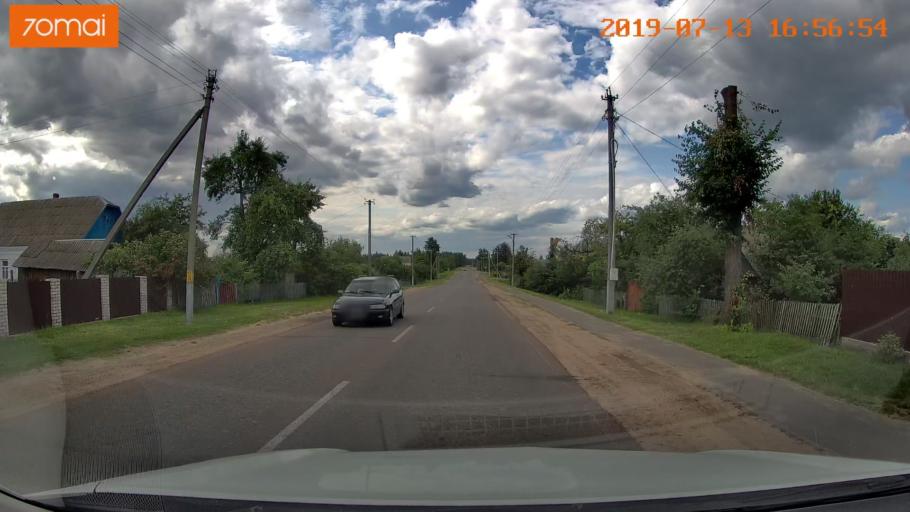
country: BY
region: Mogilev
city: Kirawsk
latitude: 53.2760
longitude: 29.4563
